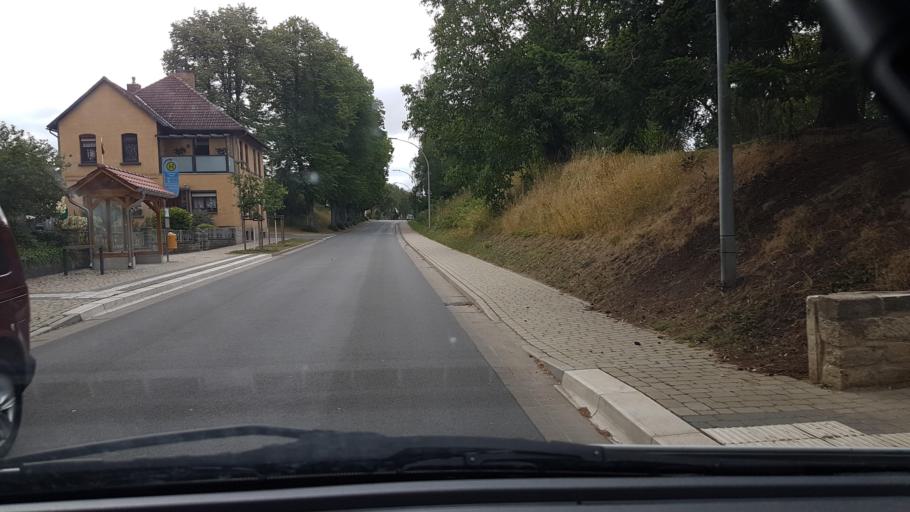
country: DE
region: Lower Saxony
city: Frellstedt
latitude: 52.2059
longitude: 10.9154
